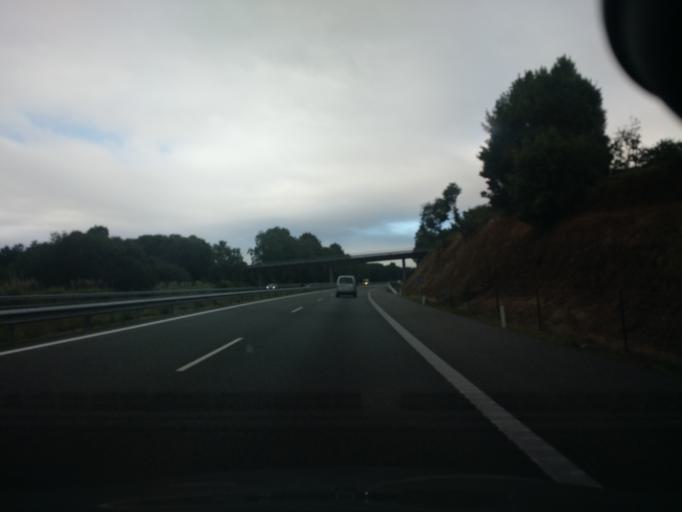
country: ES
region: Galicia
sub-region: Provincia da Coruna
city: Abegondo
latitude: 43.2124
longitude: -8.2779
